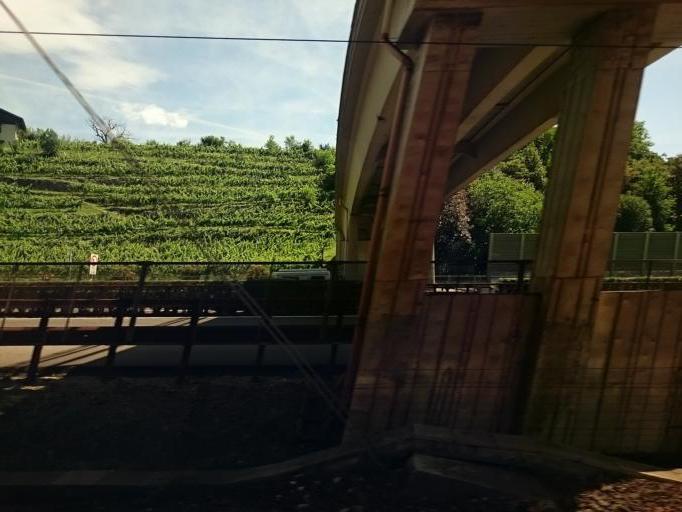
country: IT
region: Trentino-Alto Adige
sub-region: Bolzano
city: Varna
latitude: 46.7452
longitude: 11.6379
